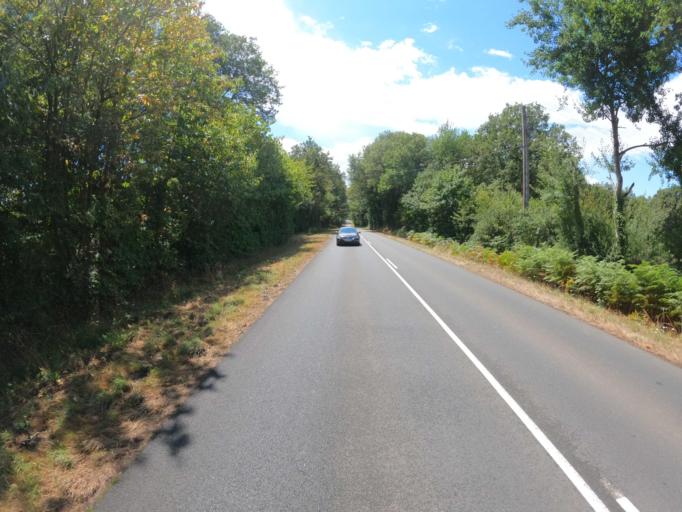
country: FR
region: Pays de la Loire
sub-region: Departement de Maine-et-Loire
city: Champigne
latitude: 47.6235
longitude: -0.5826
